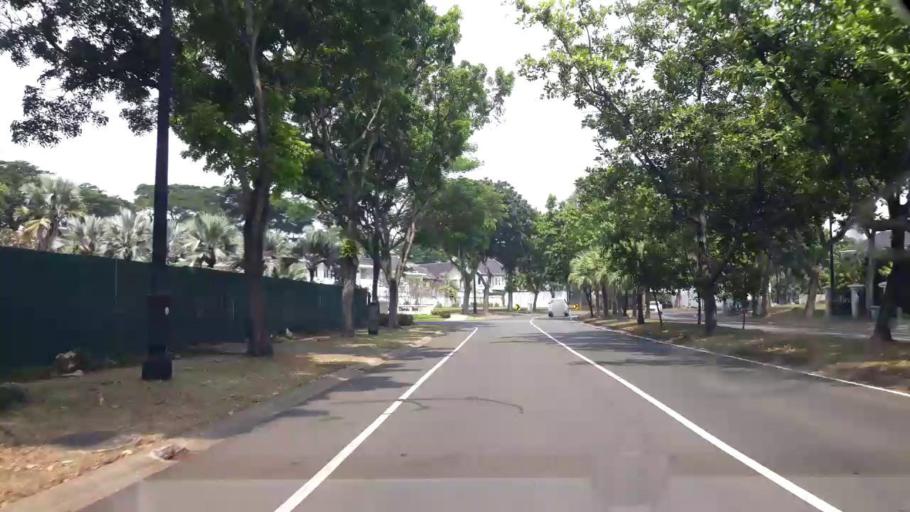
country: ID
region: Banten
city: Curug
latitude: -6.2404
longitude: 106.6049
